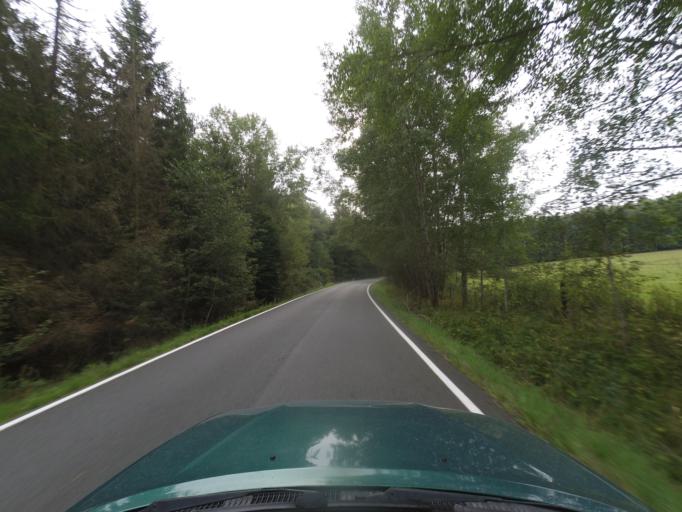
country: DE
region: Bavaria
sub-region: Upper Palatinate
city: Stadlern
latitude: 49.5885
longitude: 12.6180
